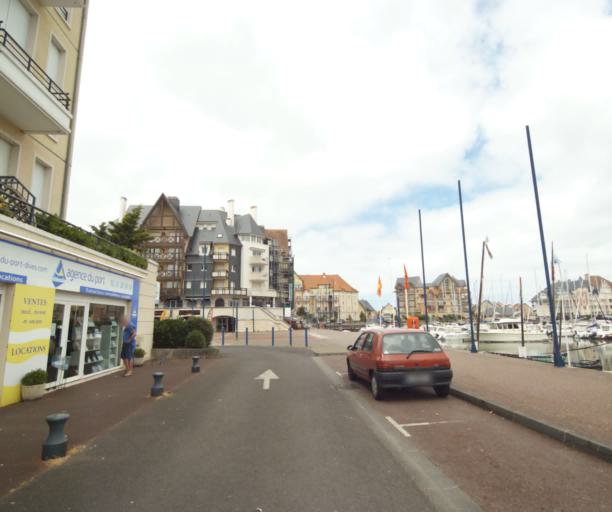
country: FR
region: Lower Normandy
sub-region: Departement du Calvados
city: Dives-sur-Mer
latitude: 49.2930
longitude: -0.0995
